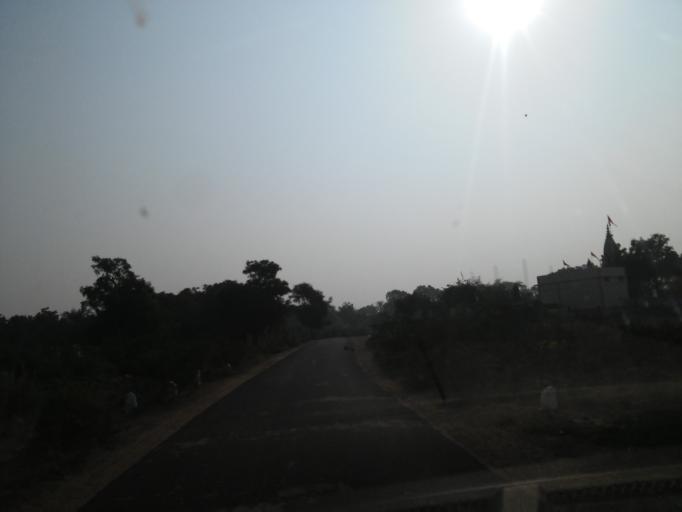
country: IN
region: Gujarat
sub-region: Kachchh
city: Mandvi
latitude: 22.8381
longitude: 69.5274
